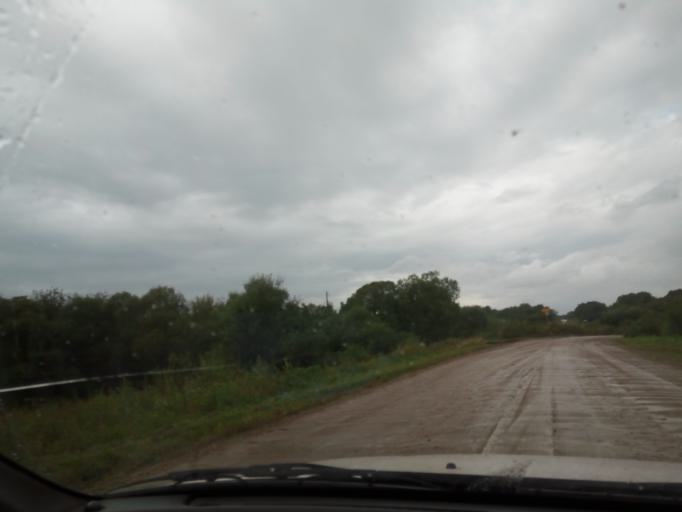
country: RU
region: Primorskiy
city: Lazo
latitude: 45.8521
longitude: 133.6461
